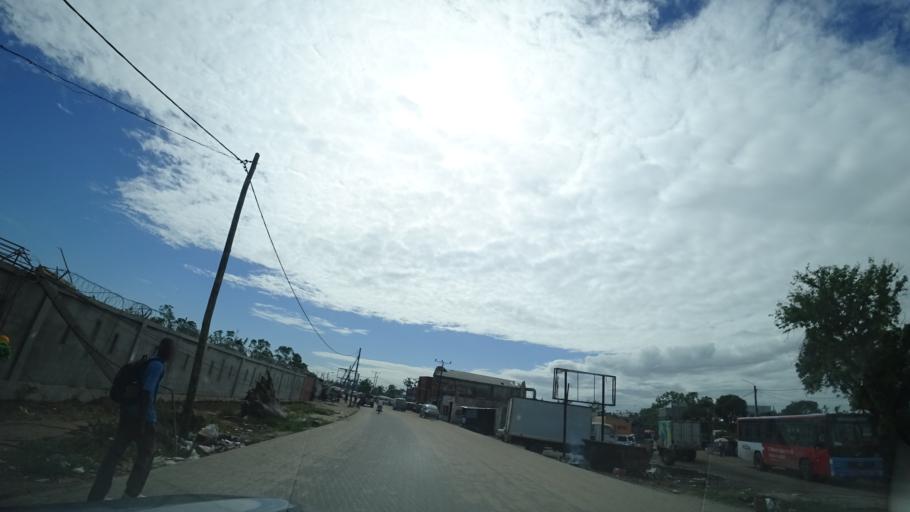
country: MZ
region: Sofala
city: Beira
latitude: -19.7535
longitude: 34.8596
